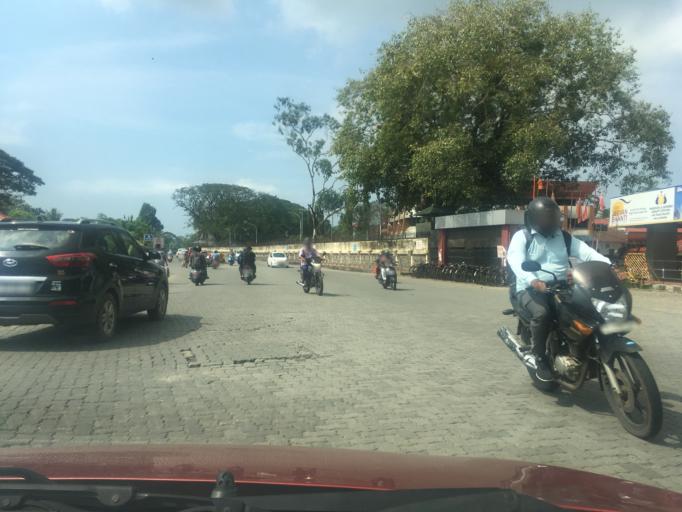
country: IN
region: Kerala
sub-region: Ernakulam
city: Cochin
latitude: 9.9446
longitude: 76.2841
